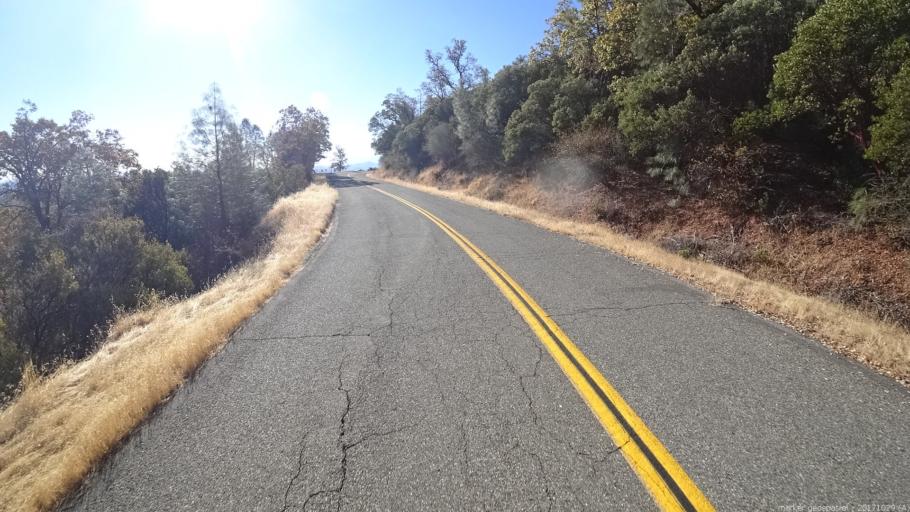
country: US
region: California
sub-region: Trinity County
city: Lewiston
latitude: 40.3704
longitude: -122.8473
